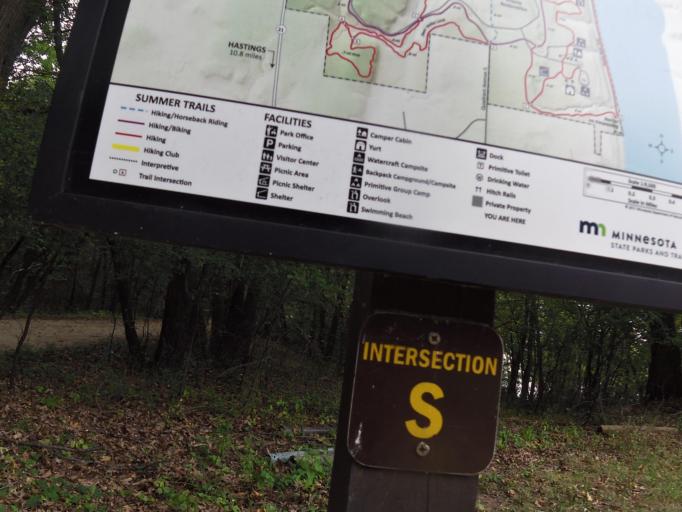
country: US
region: Minnesota
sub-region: Washington County
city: Afton
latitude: 44.8632
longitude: -92.7735
